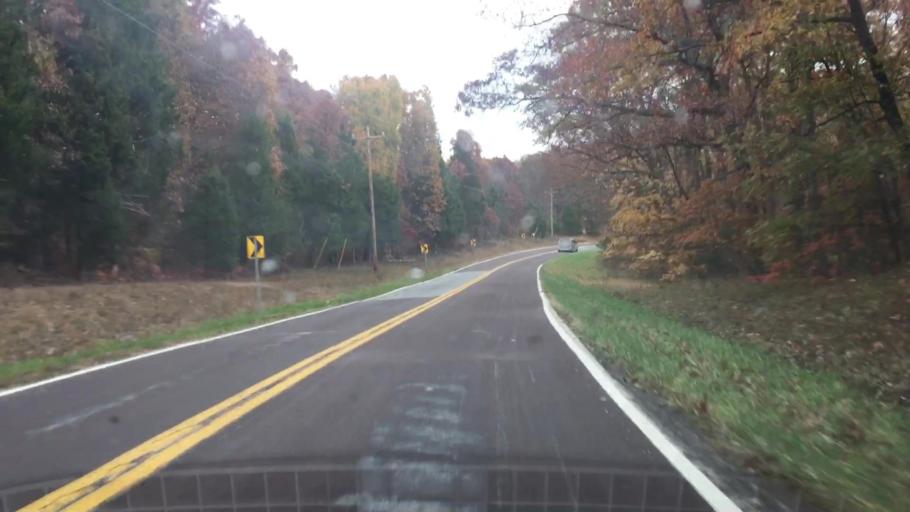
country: US
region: Missouri
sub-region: Callaway County
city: Fulton
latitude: 38.7818
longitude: -91.8284
